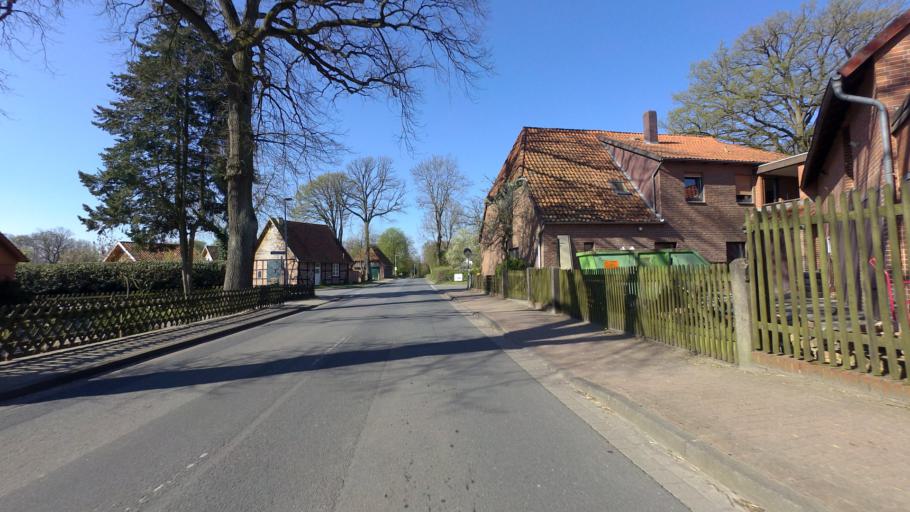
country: DE
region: Lower Saxony
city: Stockse
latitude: 52.6435
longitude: 9.3453
